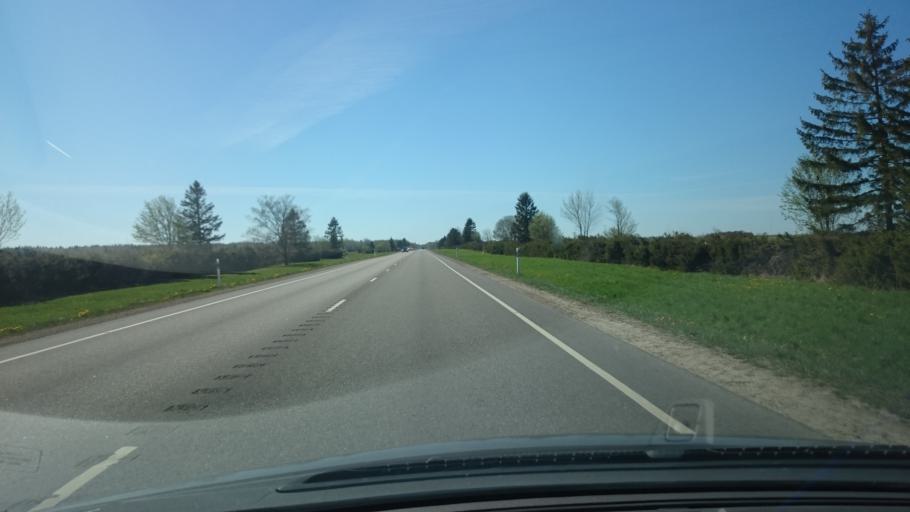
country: EE
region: Ida-Virumaa
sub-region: Sillamaee linn
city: Sillamae
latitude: 59.3920
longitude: 27.6881
